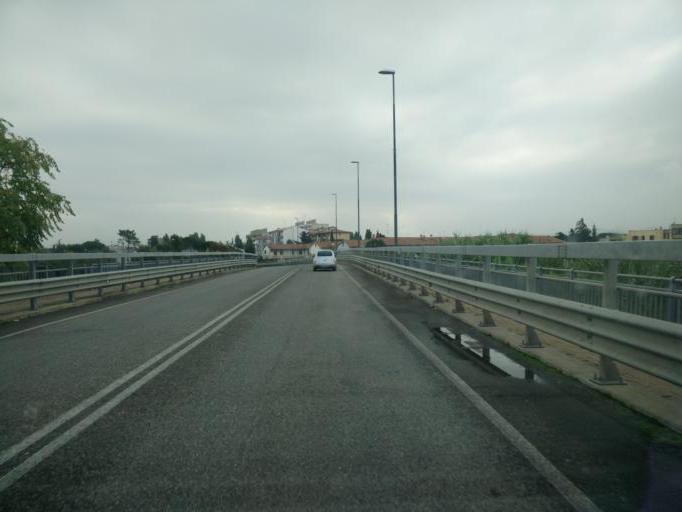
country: IT
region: Tuscany
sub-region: Province of Florence
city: Campi Bisenzio
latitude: 43.8283
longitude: 11.1386
